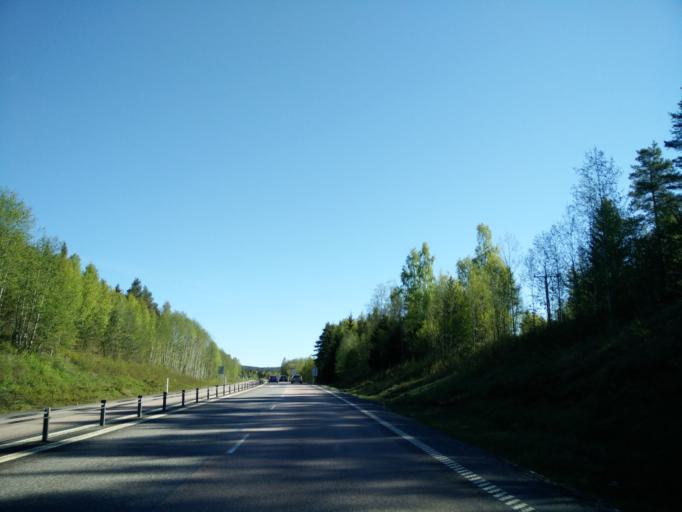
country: SE
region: Vaesternorrland
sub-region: Haernoesands Kommun
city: Haernoesand
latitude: 62.8644
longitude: 18.0353
